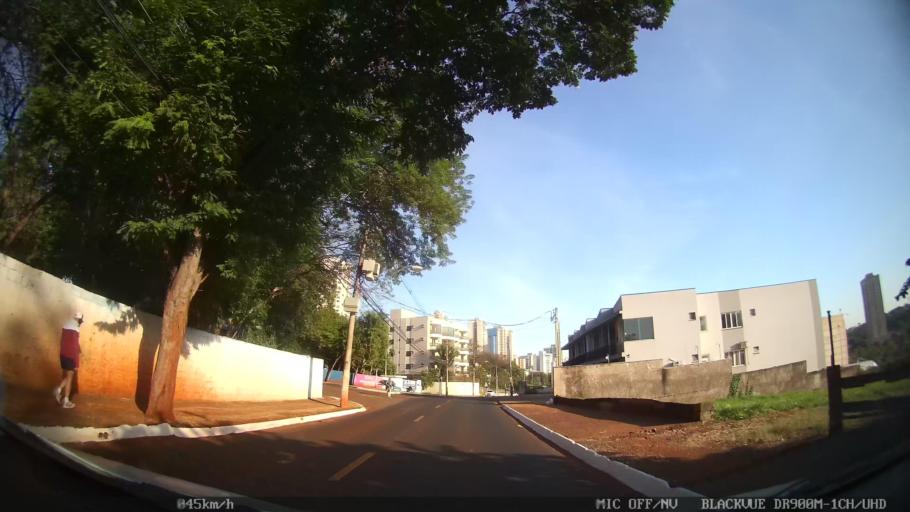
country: BR
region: Sao Paulo
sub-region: Ribeirao Preto
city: Ribeirao Preto
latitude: -21.2104
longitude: -47.7898
